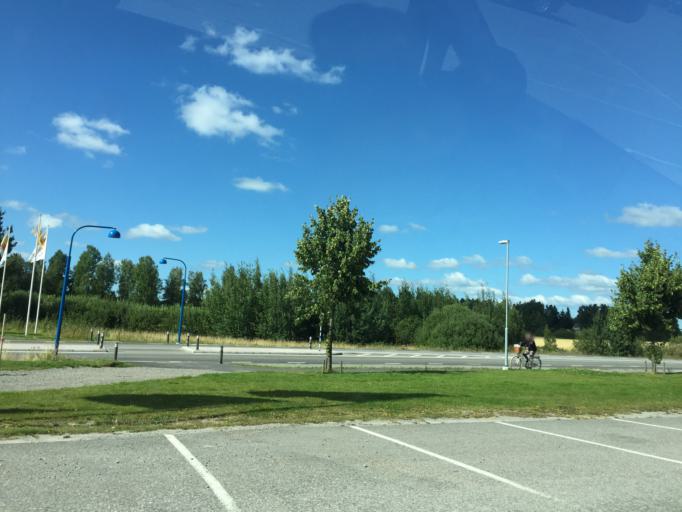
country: SE
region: Soedermanland
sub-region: Katrineholms Kommun
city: Katrineholm
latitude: 59.0040
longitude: 16.2261
